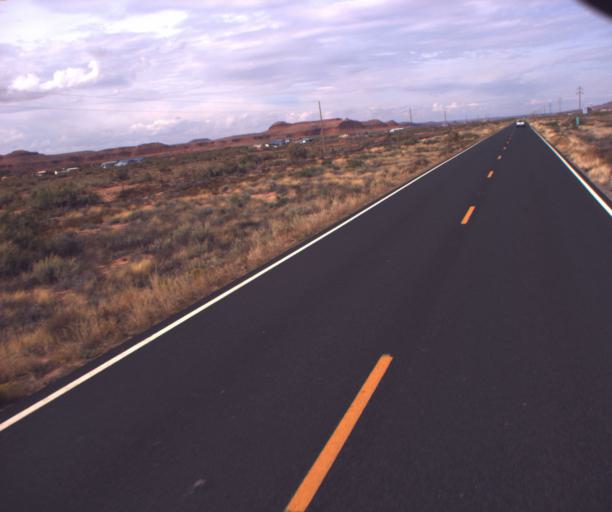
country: US
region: Arizona
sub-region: Apache County
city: Many Farms
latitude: 36.6896
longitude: -109.6090
